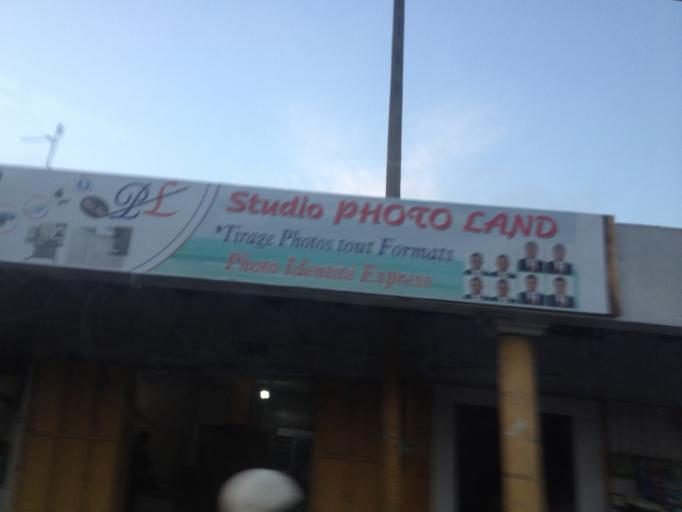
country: BJ
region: Littoral
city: Cotonou
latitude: 6.3737
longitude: 2.4418
